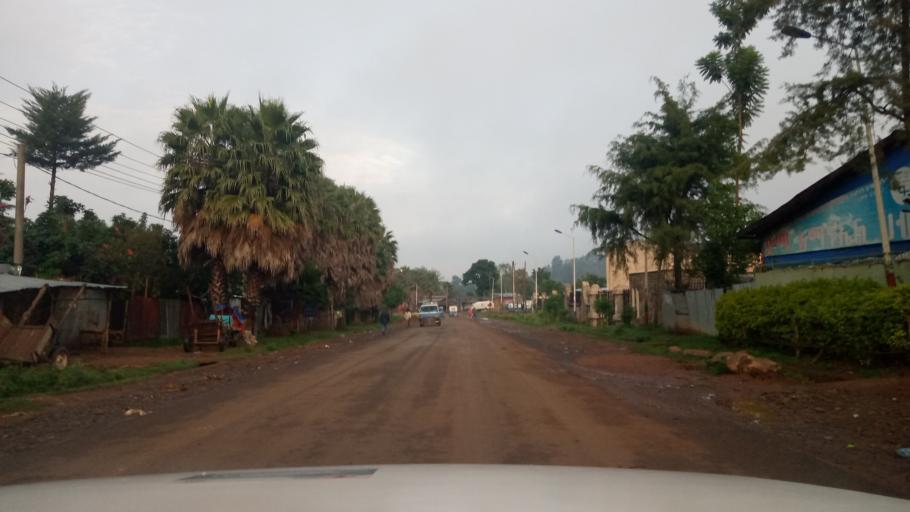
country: ET
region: Oromiya
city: Jima
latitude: 7.6829
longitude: 36.8435
